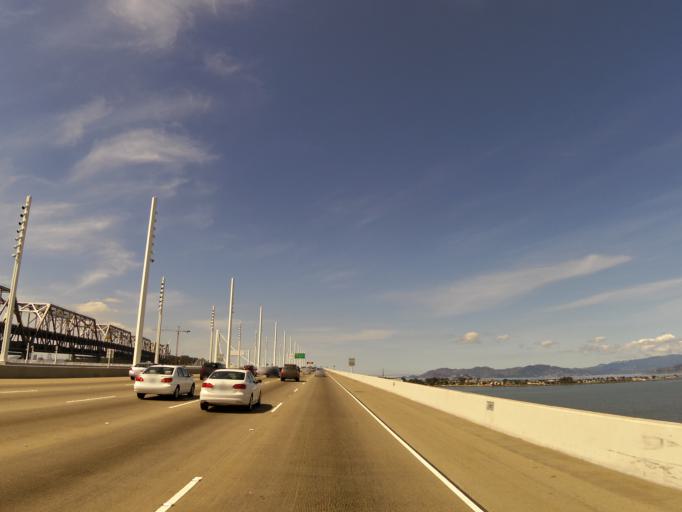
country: US
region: California
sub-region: Alameda County
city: Emeryville
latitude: 37.8201
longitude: -122.3434
